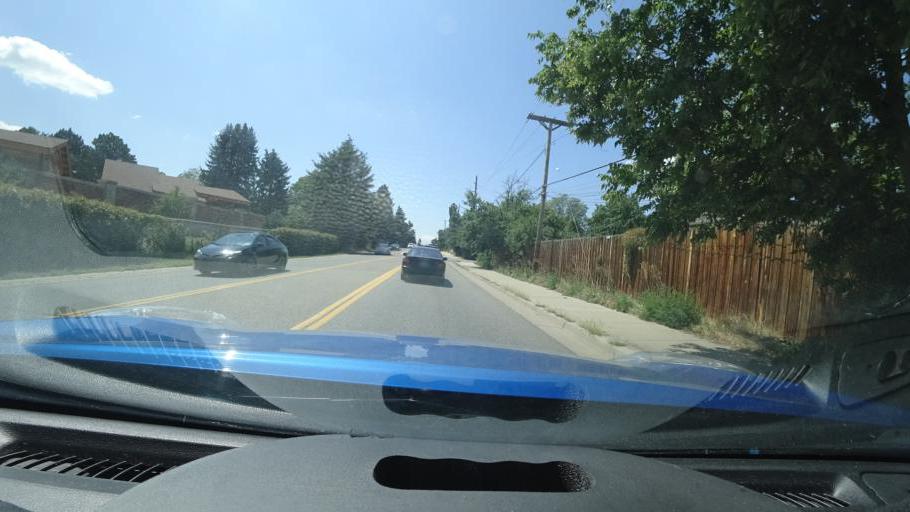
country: US
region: Colorado
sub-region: Arapahoe County
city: Glendale
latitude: 39.7080
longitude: -104.9035
